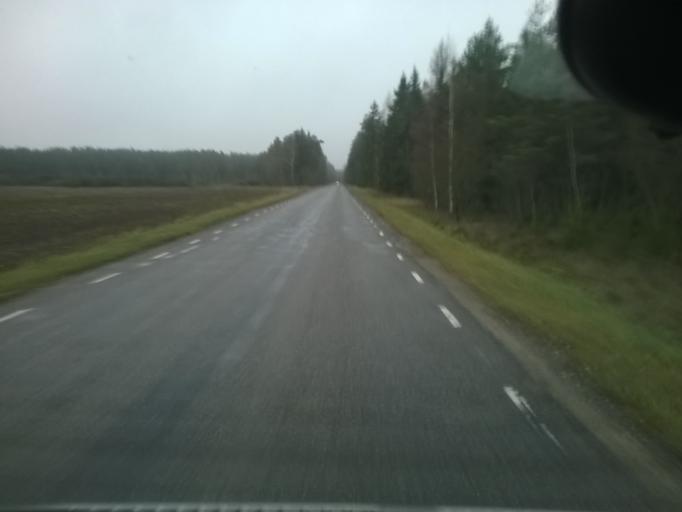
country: EE
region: Raplamaa
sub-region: Kohila vald
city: Kohila
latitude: 59.1866
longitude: 24.6610
